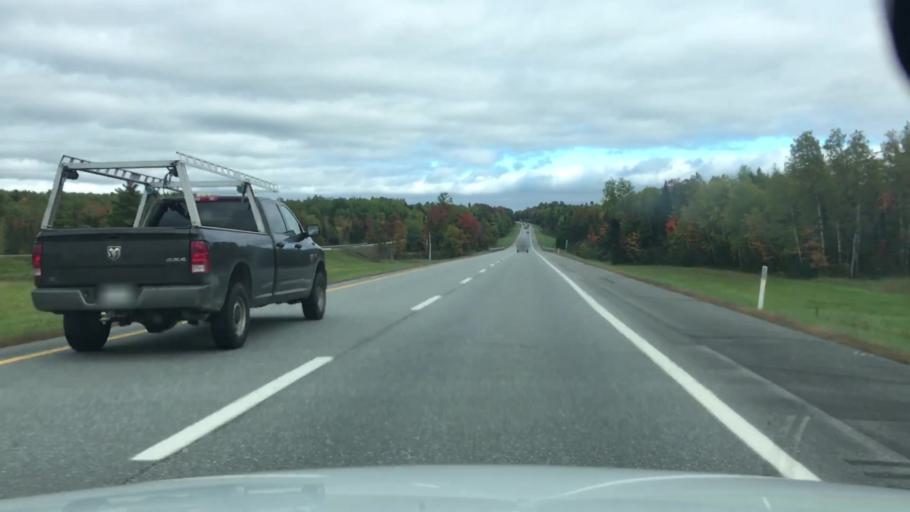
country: US
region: Maine
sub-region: Penobscot County
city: Carmel
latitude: 44.7760
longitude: -69.0470
